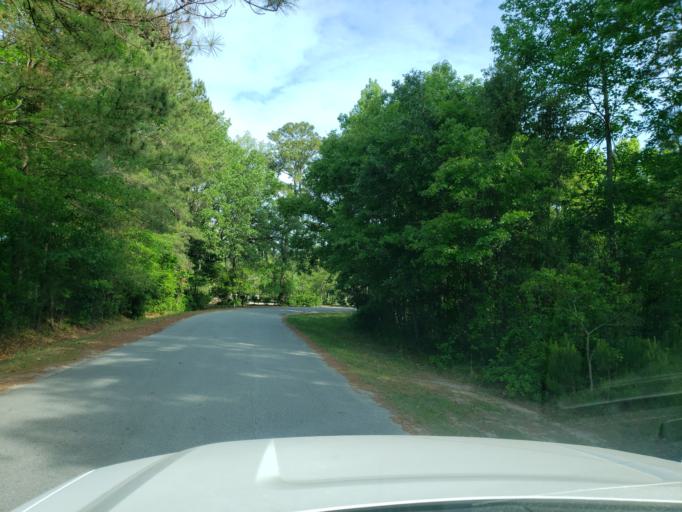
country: US
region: Georgia
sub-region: Chatham County
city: Georgetown
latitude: 32.0065
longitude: -81.2311
